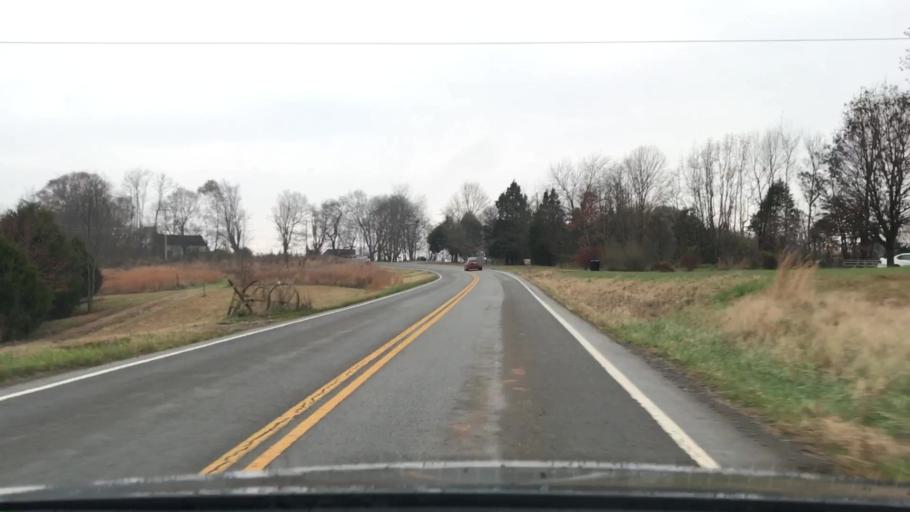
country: US
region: Tennessee
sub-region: Sumner County
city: Portland
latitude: 36.6951
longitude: -86.3853
